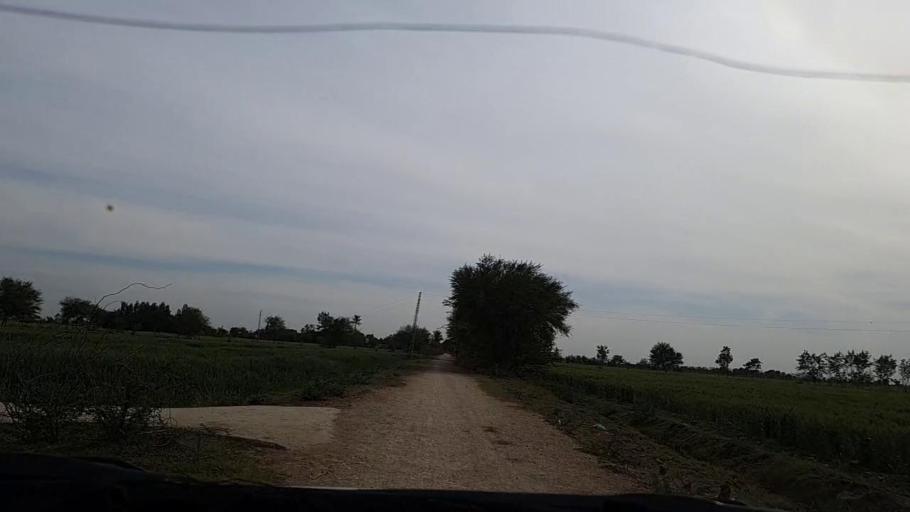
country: PK
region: Sindh
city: Dhoro Naro
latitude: 25.5157
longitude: 69.5159
